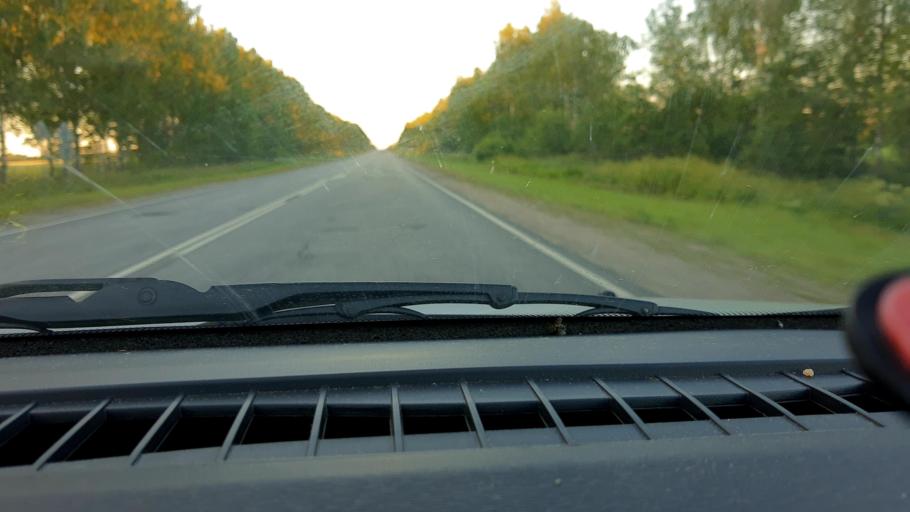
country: RU
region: Nizjnij Novgorod
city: Vladimirskoye
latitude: 56.9159
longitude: 45.0531
